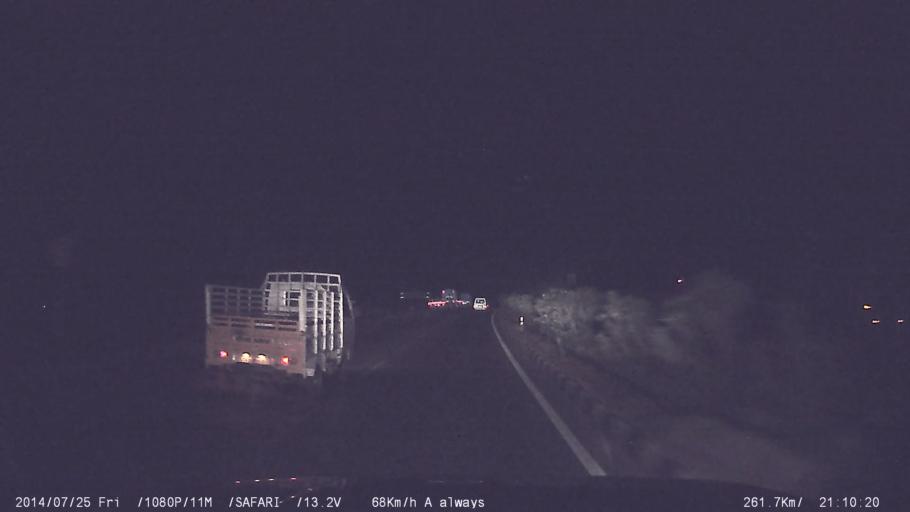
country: IN
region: Tamil Nadu
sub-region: Erode
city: Bhavani
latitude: 11.3814
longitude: 77.6546
